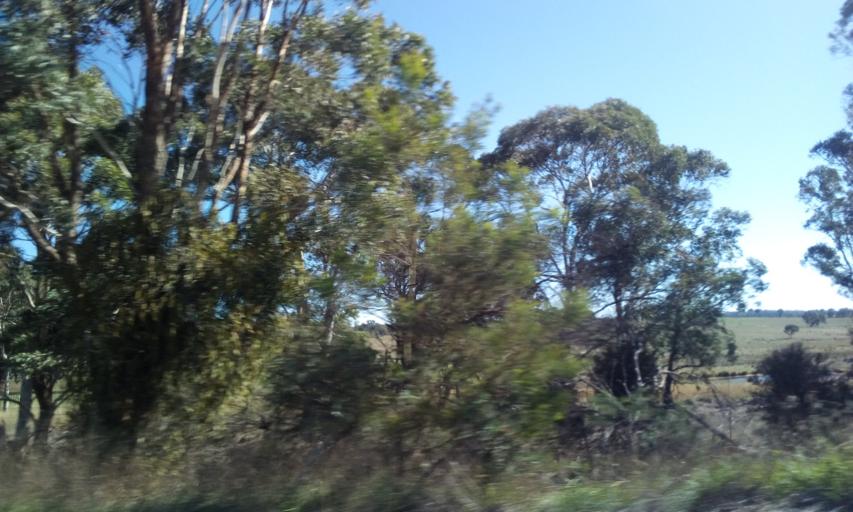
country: AU
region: New South Wales
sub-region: Yass Valley
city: Gundaroo
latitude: -35.1338
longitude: 149.3401
